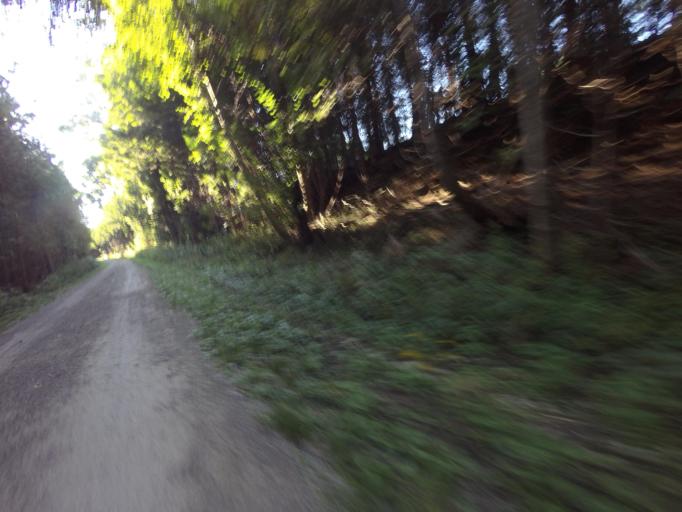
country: CA
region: Ontario
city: Goderich
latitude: 43.7603
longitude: -81.6939
